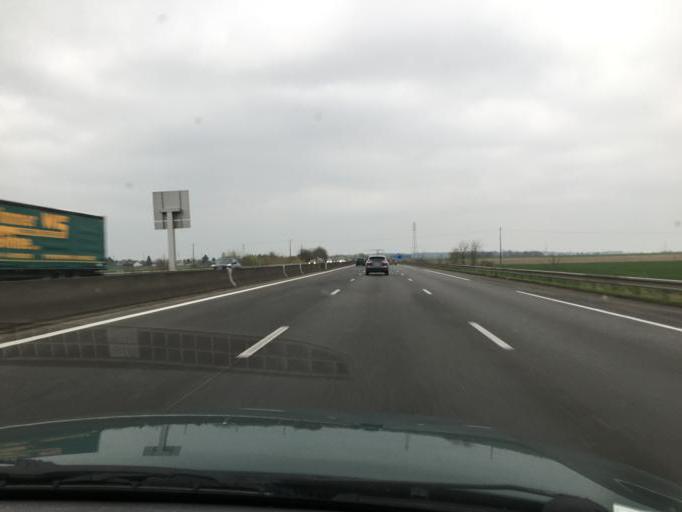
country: FR
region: Centre
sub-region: Departement du Loiret
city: La Chapelle-Saint-Mesmin
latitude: 47.9002
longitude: 1.8301
